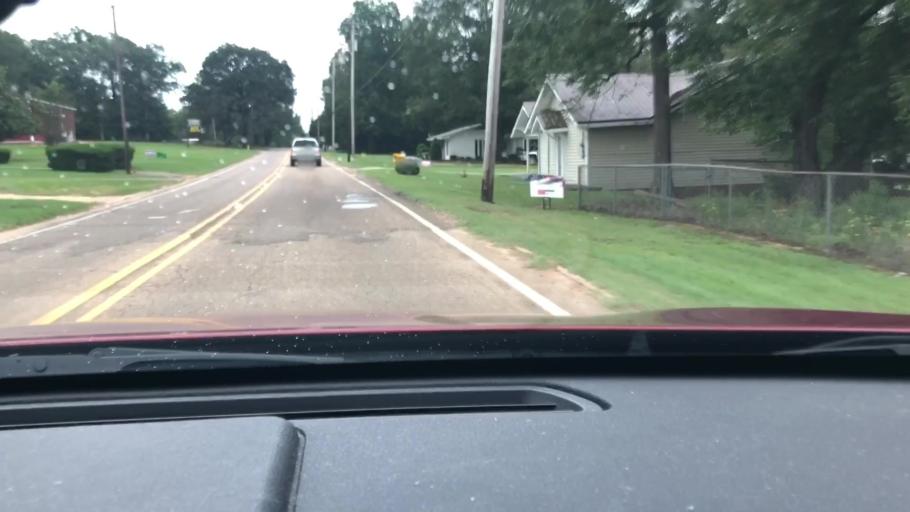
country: US
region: Arkansas
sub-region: Lafayette County
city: Stamps
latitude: 33.3659
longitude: -93.5083
